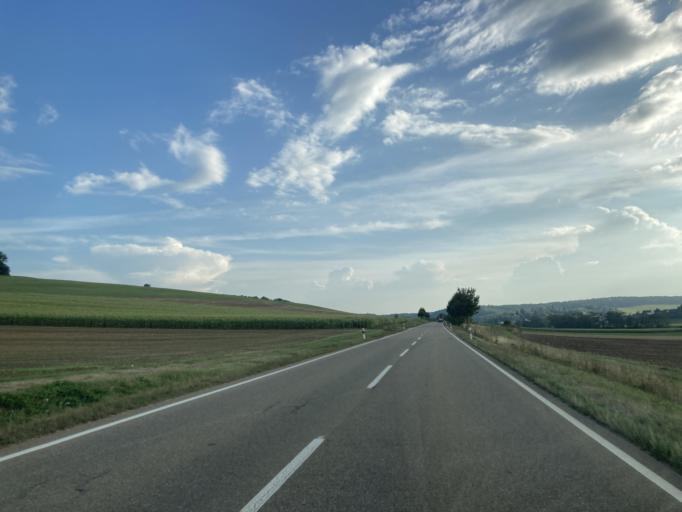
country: DE
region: Baden-Wuerttemberg
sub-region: Regierungsbezirk Stuttgart
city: Dischingen
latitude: 48.7088
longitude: 10.3750
